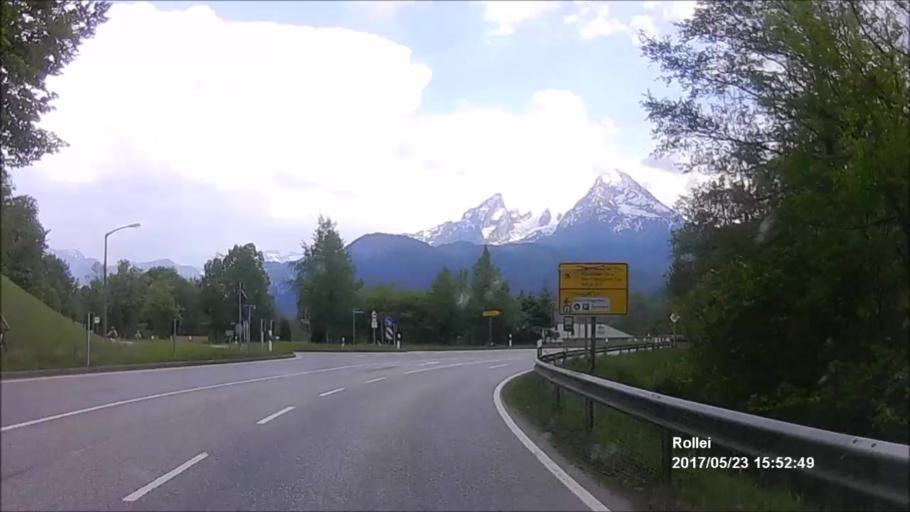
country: DE
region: Bavaria
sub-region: Upper Bavaria
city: Bischofswiesen
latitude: 47.6420
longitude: 12.9718
